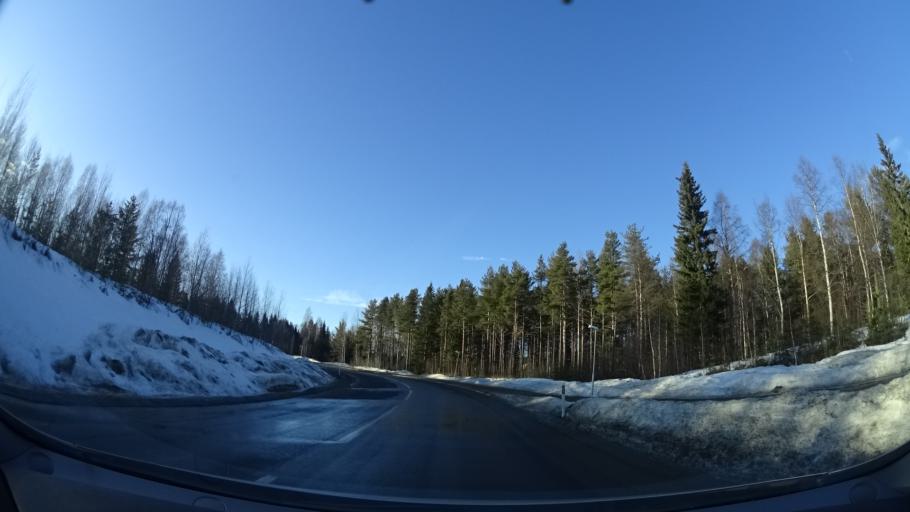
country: SE
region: Vaesterbotten
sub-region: Skelleftea Kommun
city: Byske
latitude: 64.9511
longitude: 21.1931
